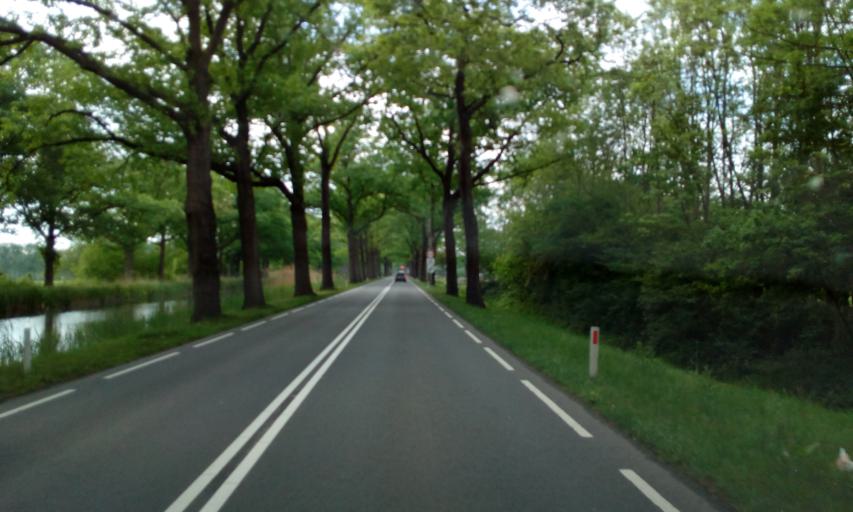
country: NL
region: Gelderland
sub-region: Gemeente Apeldoorn
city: Beekbergen
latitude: 52.1708
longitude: 5.9974
